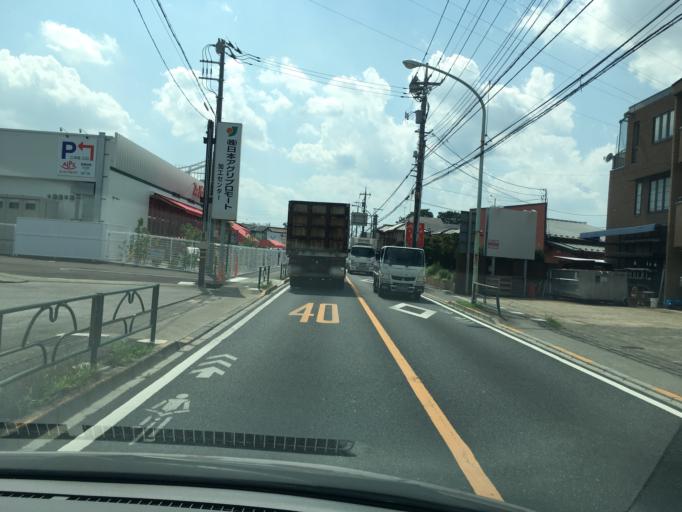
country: JP
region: Tokyo
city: Higashimurayama-shi
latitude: 35.7716
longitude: 139.4768
